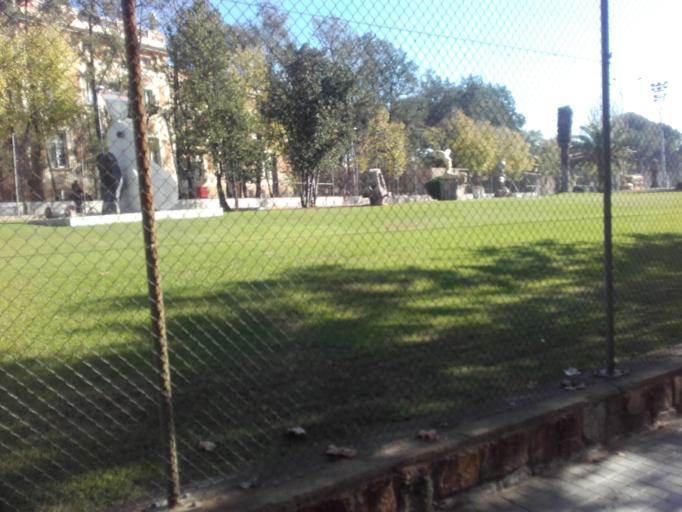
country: ES
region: Catalonia
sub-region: Provincia de Barcelona
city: les Corts
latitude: 41.3839
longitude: 2.1228
